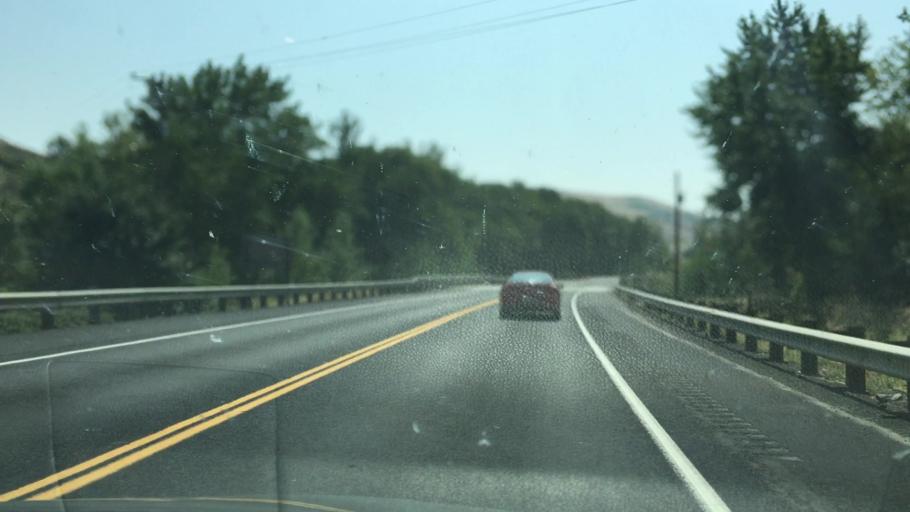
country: US
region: Idaho
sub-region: Nez Perce County
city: Lapwai
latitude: 46.4440
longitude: -116.8134
